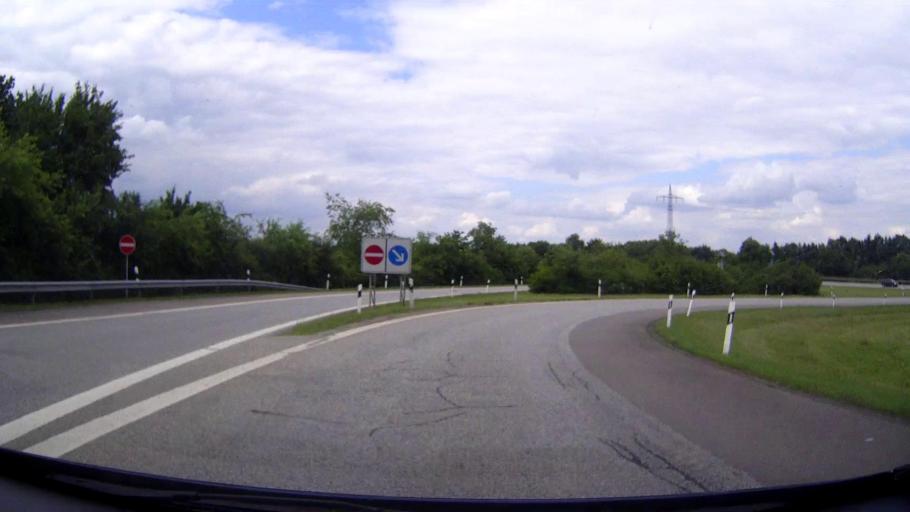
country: DE
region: Schleswig-Holstein
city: Padenstedt
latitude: 54.0709
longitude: 9.9215
